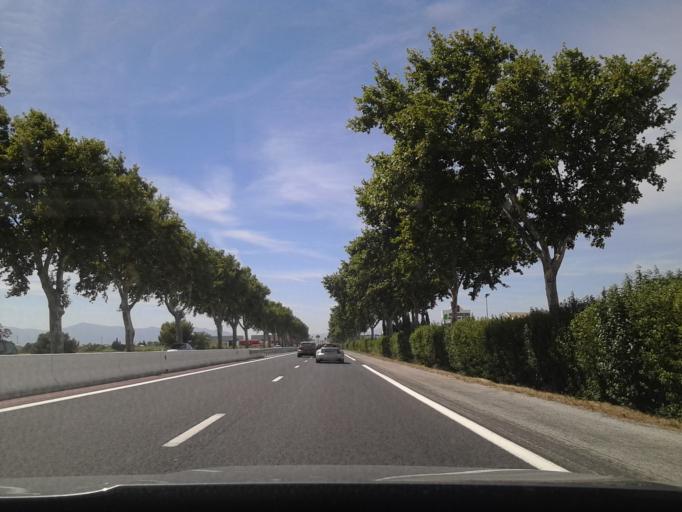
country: FR
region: Languedoc-Roussillon
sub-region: Departement des Pyrenees-Orientales
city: Rivesaltes
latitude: 42.7626
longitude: 2.8982
